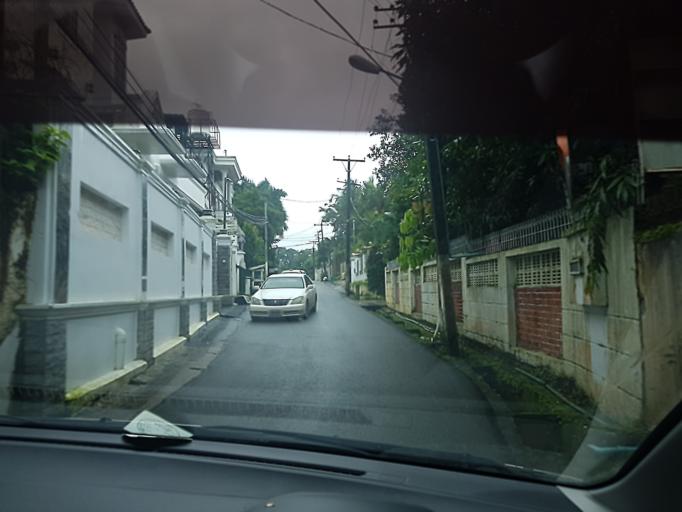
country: MM
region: Yangon
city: Yangon
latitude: 16.8125
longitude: 96.1463
